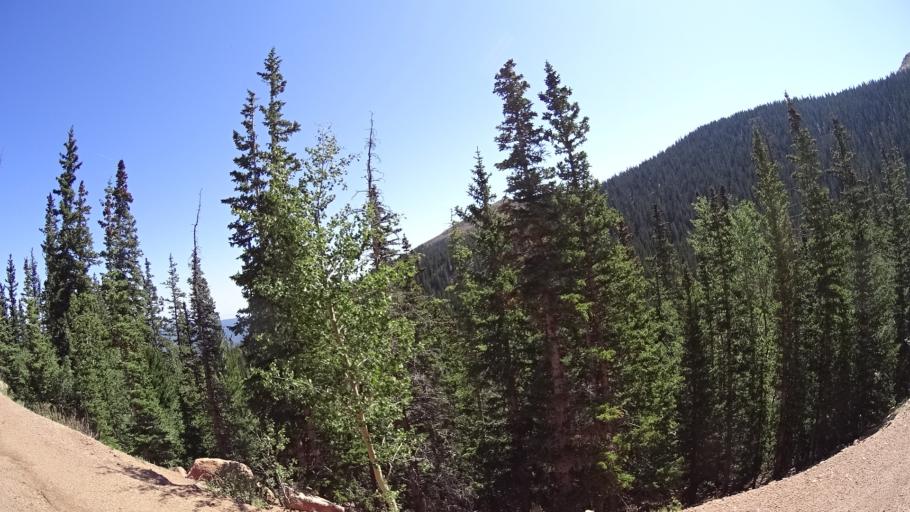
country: US
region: Colorado
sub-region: El Paso County
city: Cascade-Chipita Park
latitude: 38.8796
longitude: -105.0733
